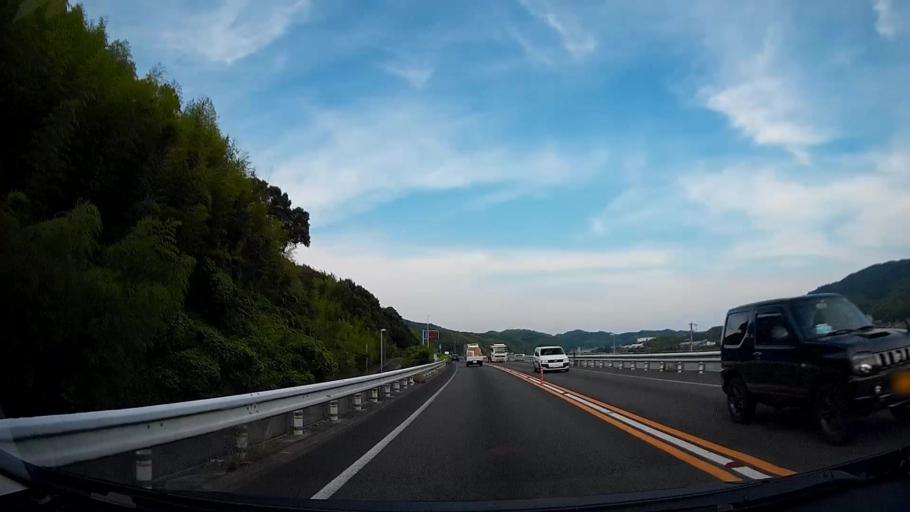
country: JP
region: Aichi
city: Nishio
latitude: 34.8614
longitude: 137.1073
